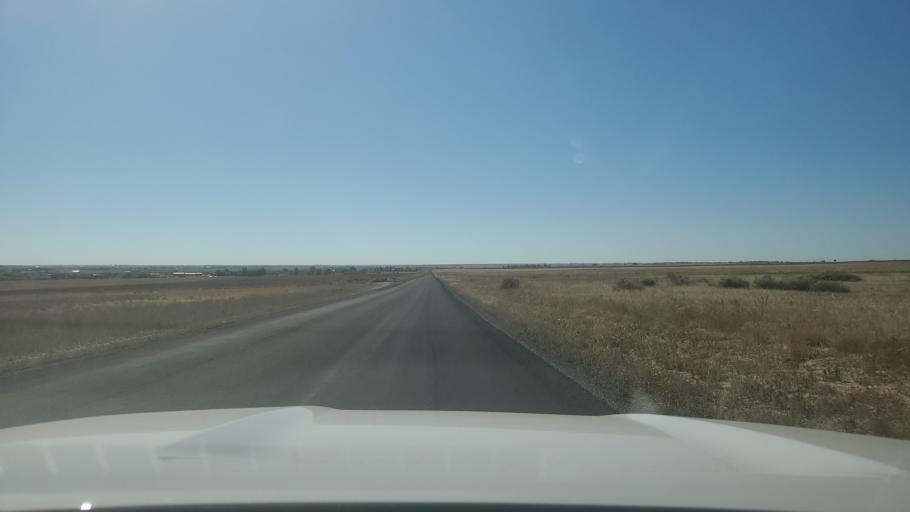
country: US
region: Colorado
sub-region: Adams County
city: Bennett
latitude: 39.7541
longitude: -104.3772
